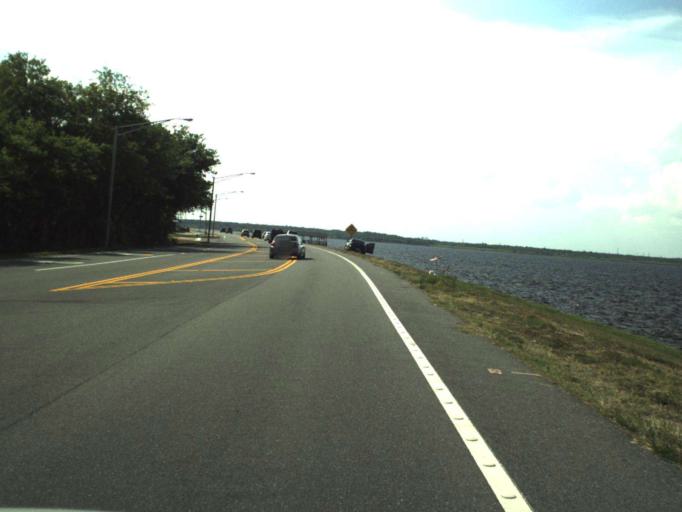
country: US
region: Florida
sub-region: Seminole County
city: Sanford
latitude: 28.8205
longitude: -81.2915
